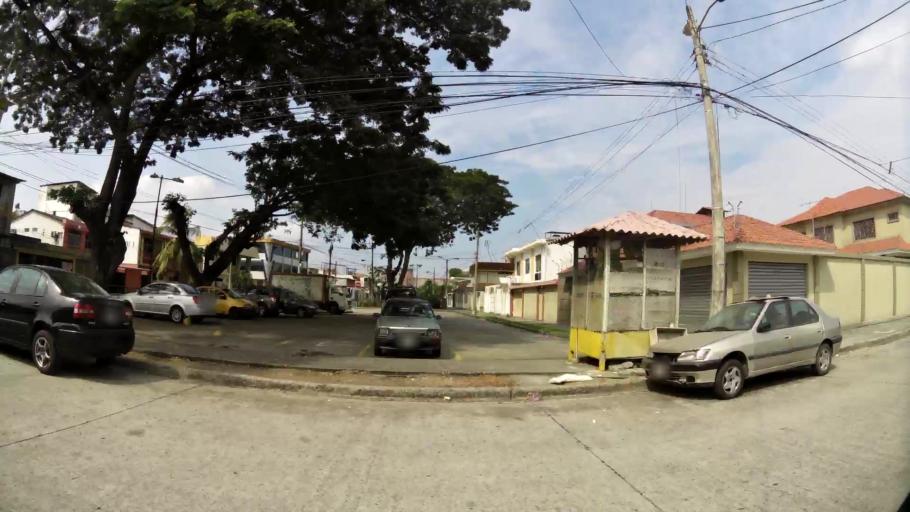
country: EC
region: Guayas
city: Guayaquil
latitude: -2.2417
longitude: -79.8986
